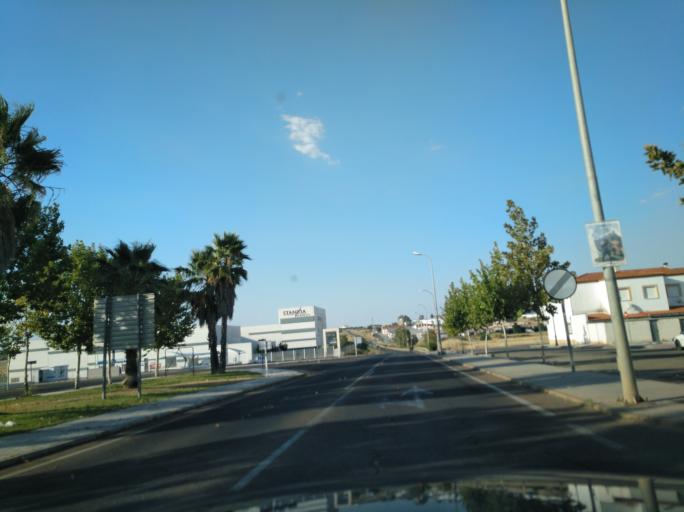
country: ES
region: Extremadura
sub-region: Provincia de Badajoz
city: Olivenza
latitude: 38.6912
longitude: -7.0928
